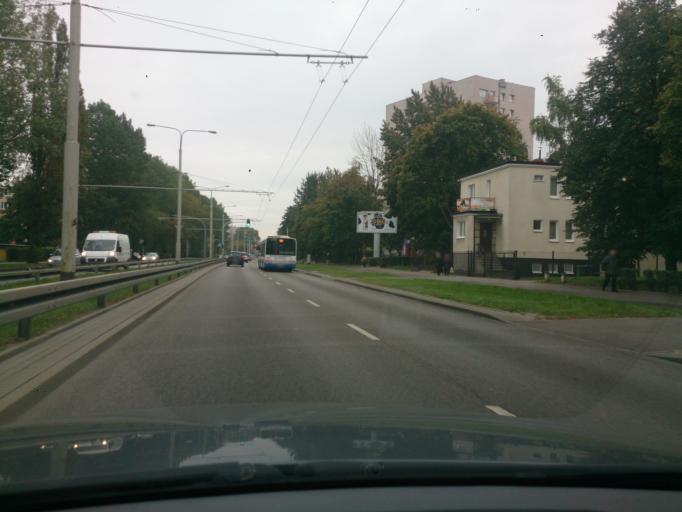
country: PL
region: Pomeranian Voivodeship
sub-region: Gdynia
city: Pogorze
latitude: 54.5401
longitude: 18.4664
